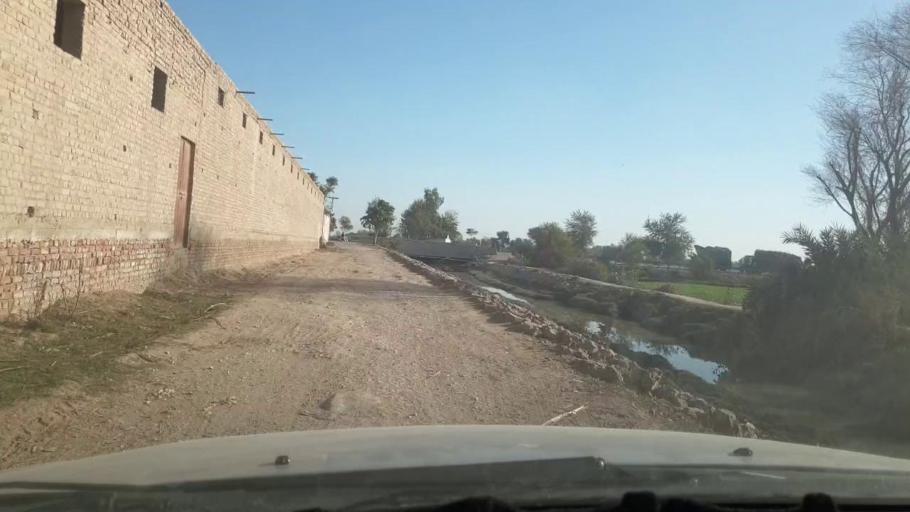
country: PK
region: Sindh
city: Adilpur
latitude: 27.9406
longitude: 69.2209
